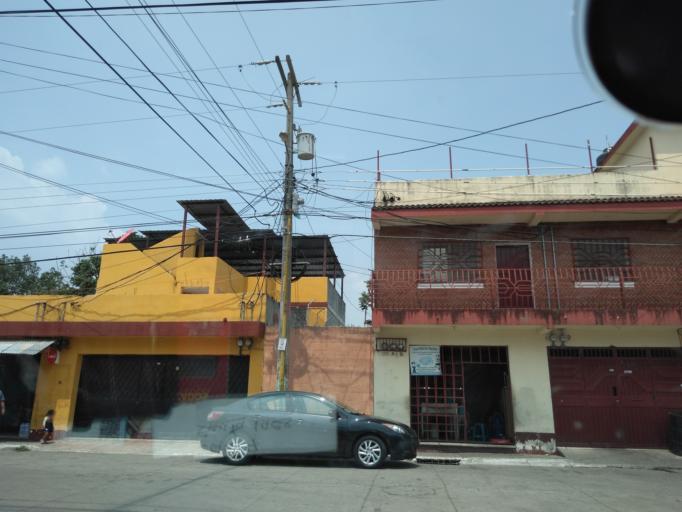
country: GT
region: Guatemala
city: Petapa
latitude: 14.5235
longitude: -90.5406
